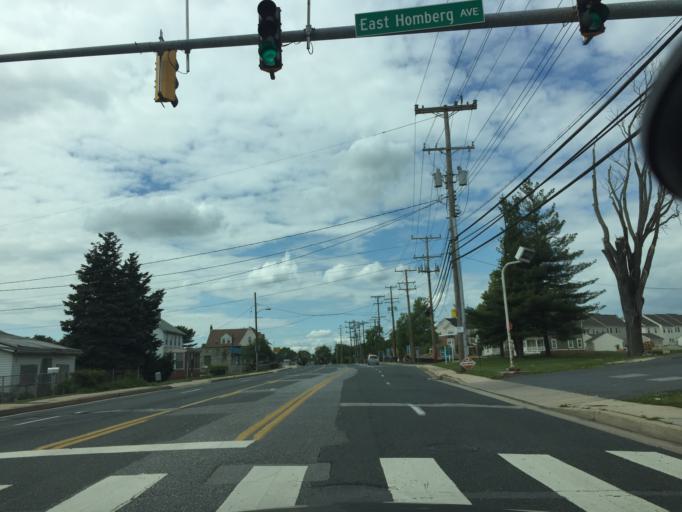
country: US
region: Maryland
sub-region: Baltimore County
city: Middle River
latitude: 39.3129
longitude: -76.4487
